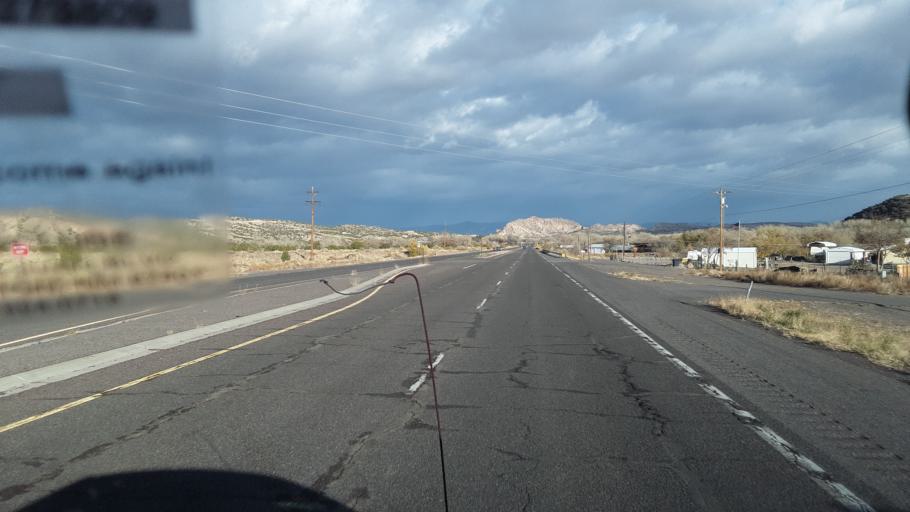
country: US
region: New Mexico
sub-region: Rio Arriba County
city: Ohkay Owingeh
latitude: 36.0795
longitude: -106.1286
